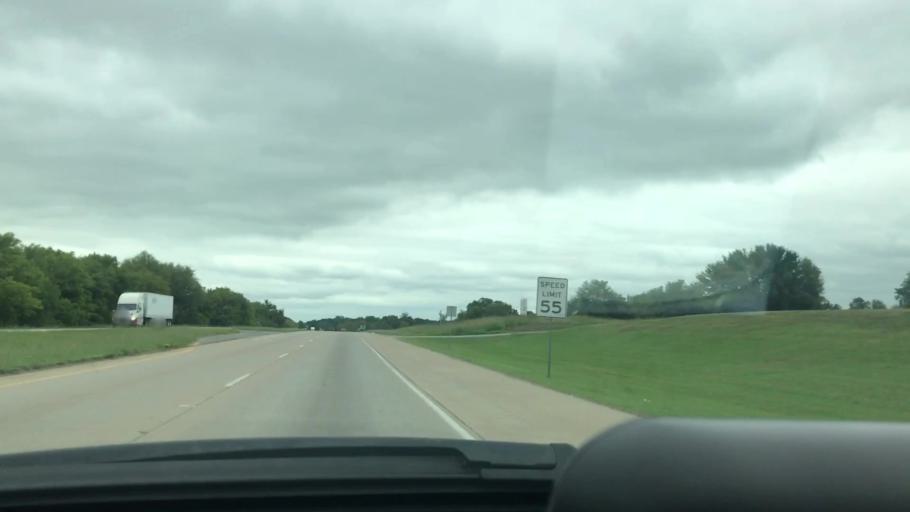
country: US
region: Oklahoma
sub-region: Mayes County
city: Chouteau
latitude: 36.1945
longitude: -95.3416
